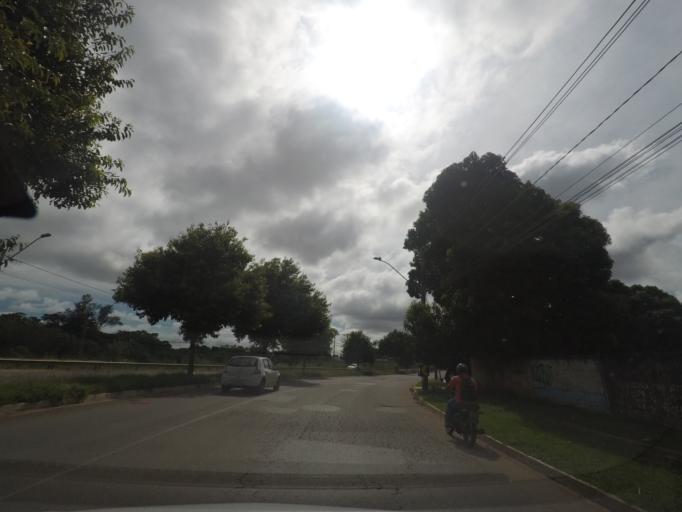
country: BR
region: Goias
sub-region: Goiania
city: Goiania
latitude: -16.6568
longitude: -49.2068
